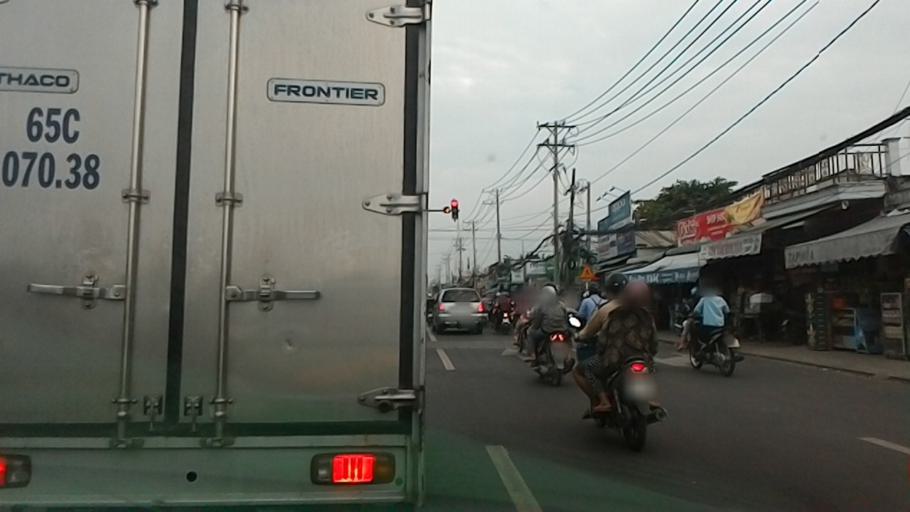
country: VN
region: Can Tho
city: Cai Rang
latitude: 10.0260
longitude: 105.7582
